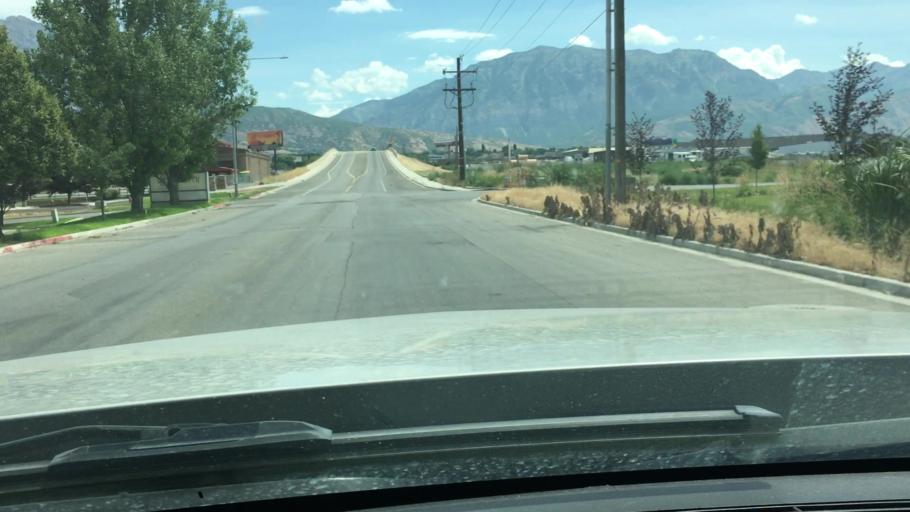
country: US
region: Utah
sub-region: Utah County
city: Lindon
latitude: 40.3335
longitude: -111.7475
